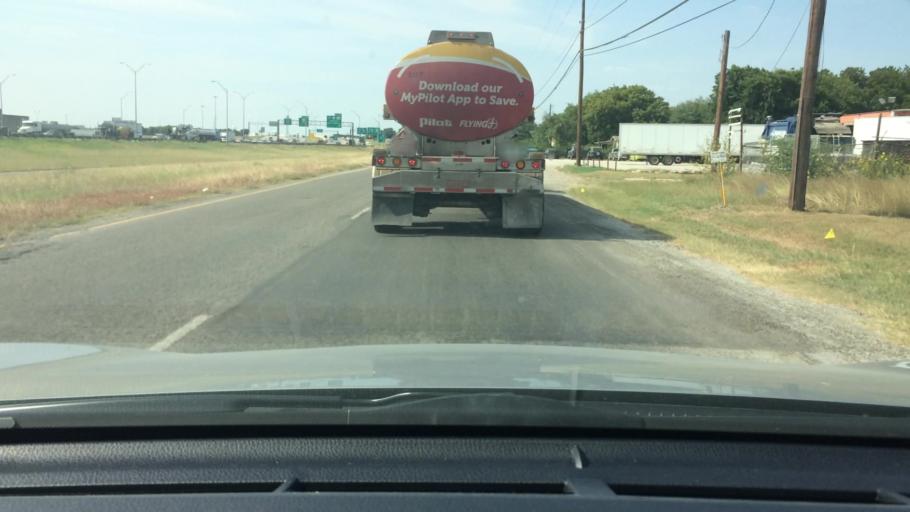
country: US
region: Texas
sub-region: Bexar County
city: Kirby
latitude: 29.4292
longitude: -98.3886
